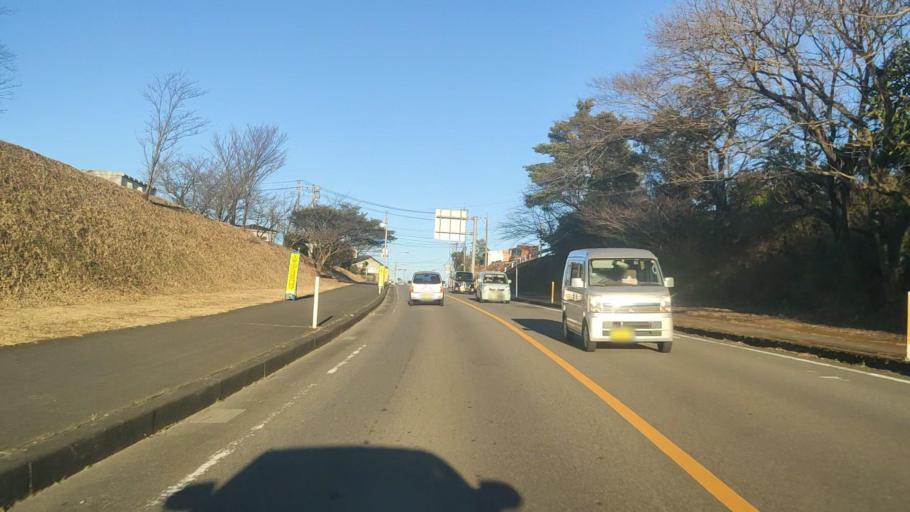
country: JP
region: Miyazaki
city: Miyazaki-shi
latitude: 31.8321
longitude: 131.3182
